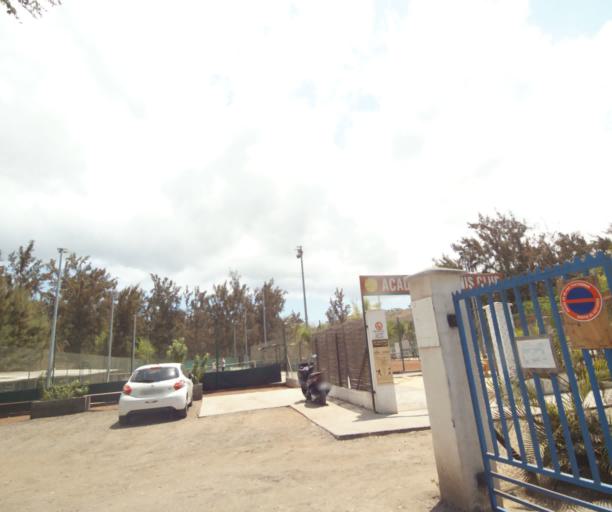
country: RE
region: Reunion
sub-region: Reunion
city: Saint-Paul
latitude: -21.0730
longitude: 55.2252
